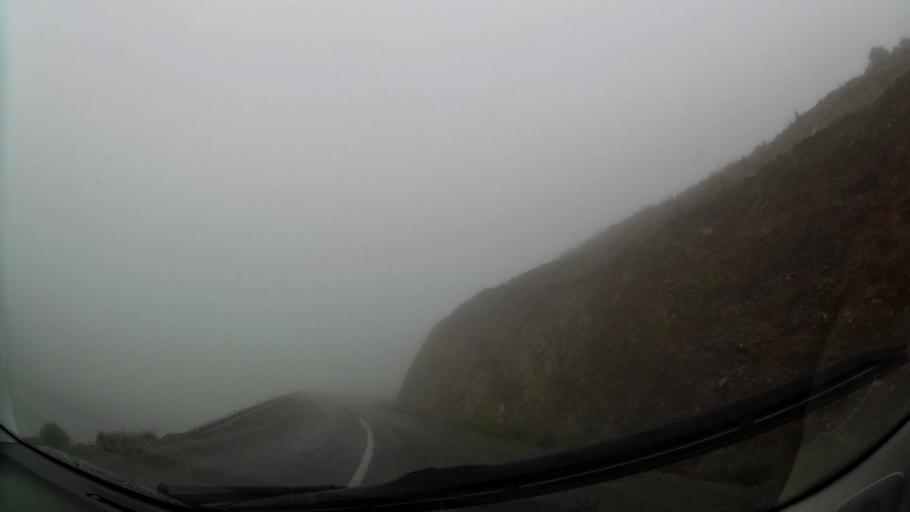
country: MA
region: Oriental
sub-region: Nador
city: Boudinar
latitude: 35.1032
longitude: -3.5547
